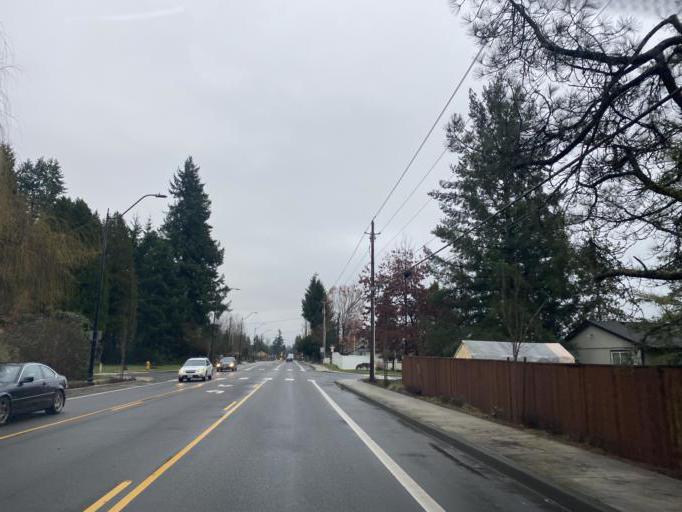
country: US
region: Washington
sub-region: Clark County
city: Battle Ground
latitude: 45.7730
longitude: -122.5373
